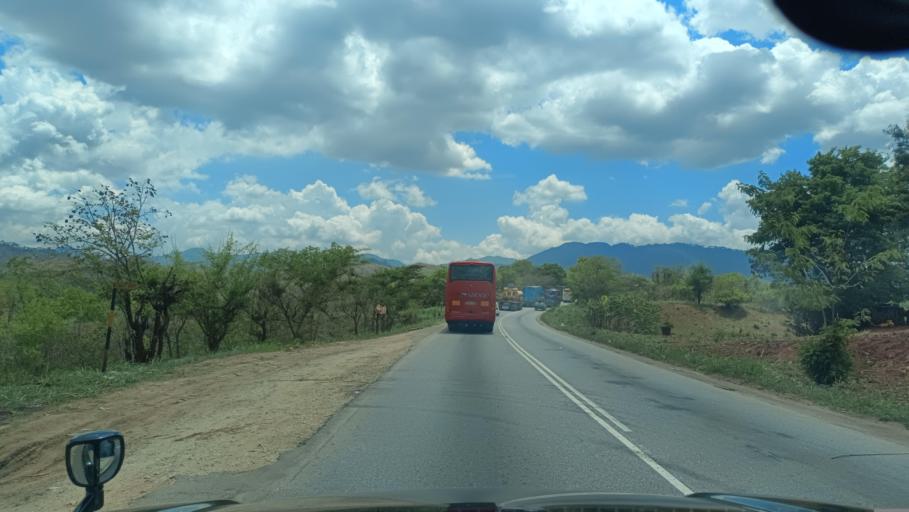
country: TZ
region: Morogoro
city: Mikumi
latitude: -7.4607
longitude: 36.9194
